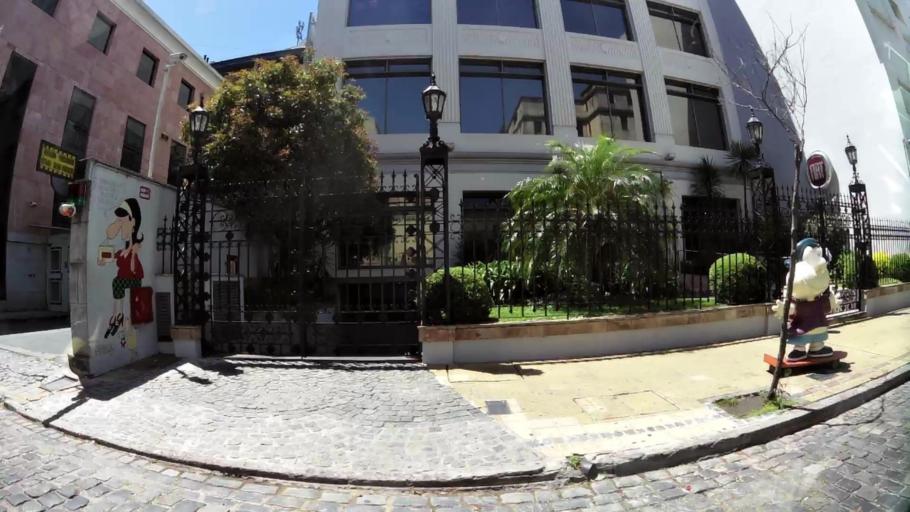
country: AR
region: Buenos Aires F.D.
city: Buenos Aires
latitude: -34.6141
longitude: -58.3706
